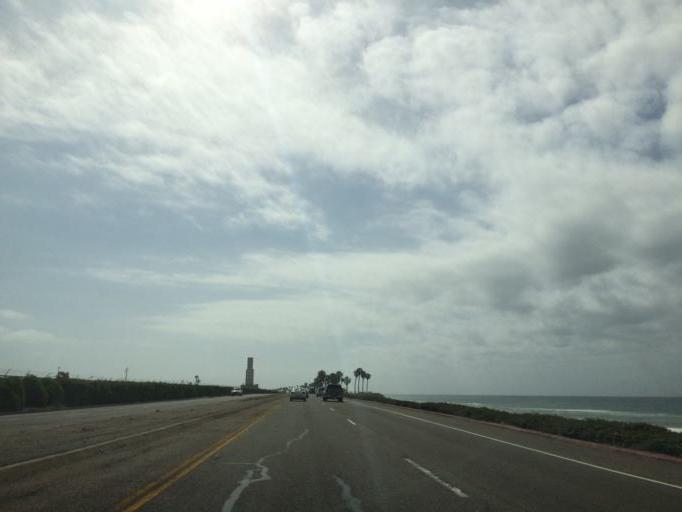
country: US
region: California
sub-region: Orange County
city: Huntington Beach
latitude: 33.6780
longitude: -118.0298
